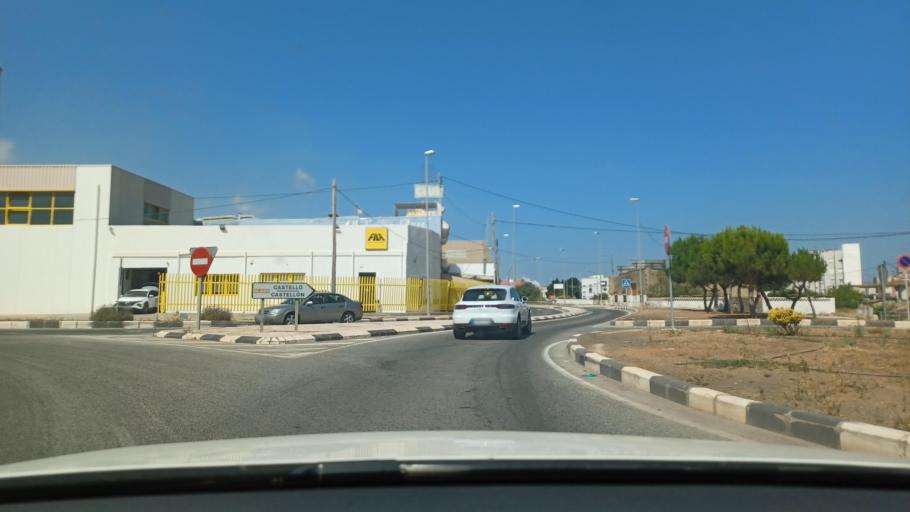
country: ES
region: Valencia
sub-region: Provincia de Castello
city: Chilches
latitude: 39.7818
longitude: -0.1928
